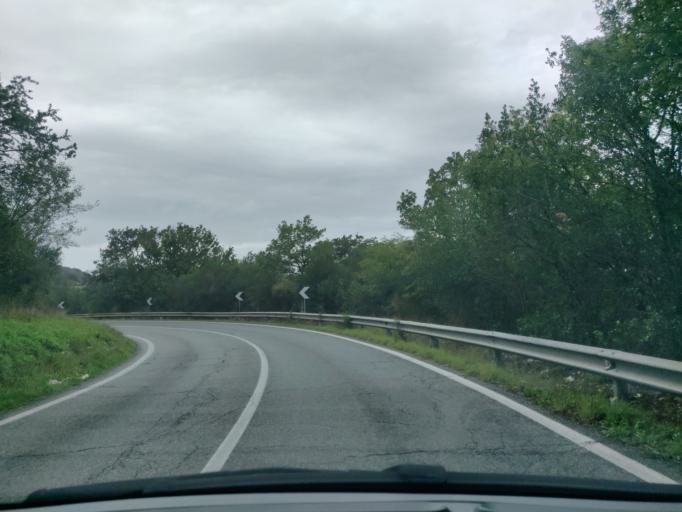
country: IT
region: Latium
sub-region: Citta metropolitana di Roma Capitale
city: Allumiere
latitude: 42.1453
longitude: 11.8889
